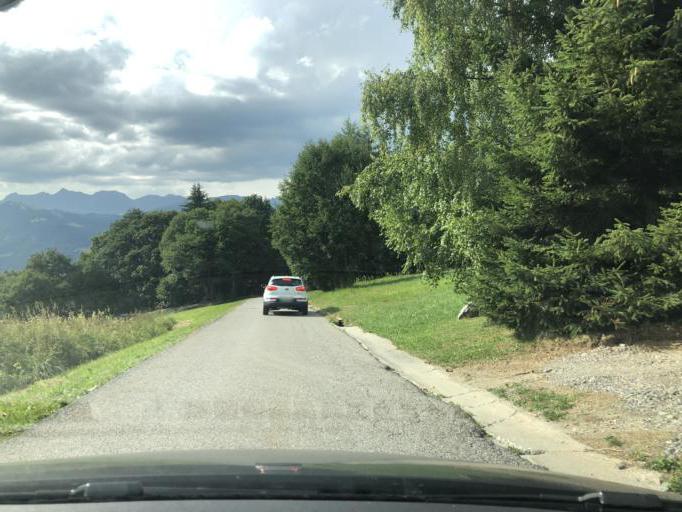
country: FR
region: Rhone-Alpes
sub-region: Departement de la Haute-Savoie
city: Megeve
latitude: 45.8392
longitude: 6.6438
